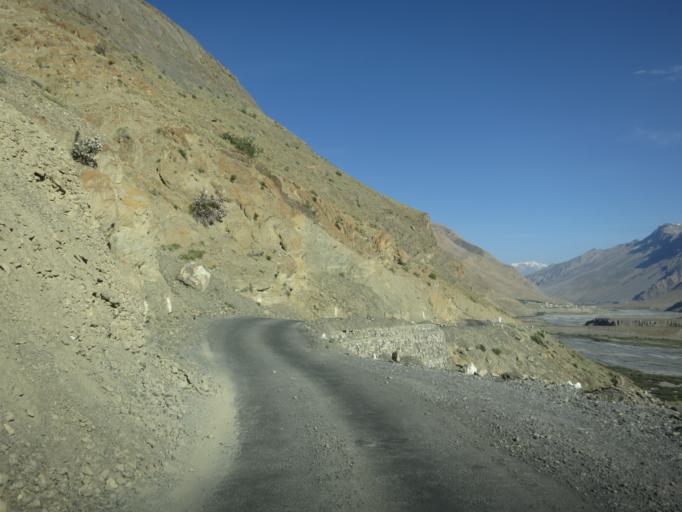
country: IN
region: Himachal Pradesh
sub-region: Shimla
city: Sarahan
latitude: 32.2594
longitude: 78.0416
